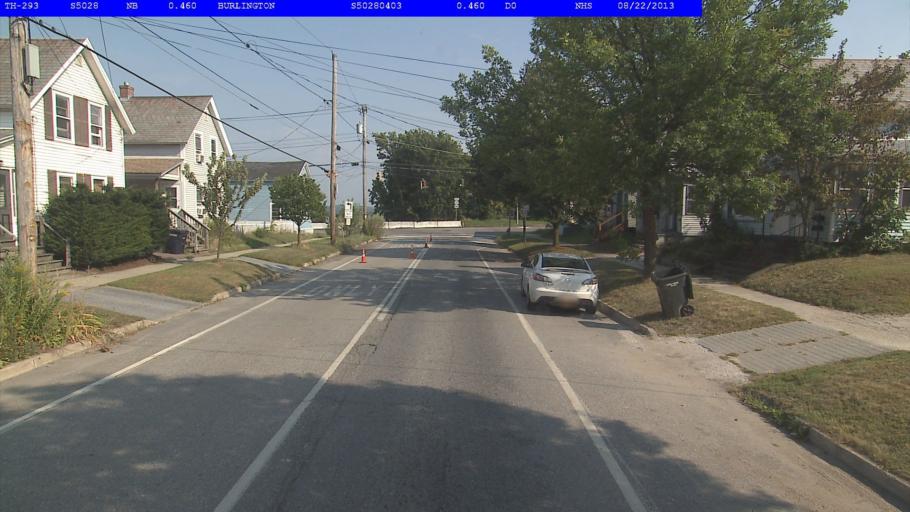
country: US
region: Vermont
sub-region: Chittenden County
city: Burlington
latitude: 44.4870
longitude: -73.2179
